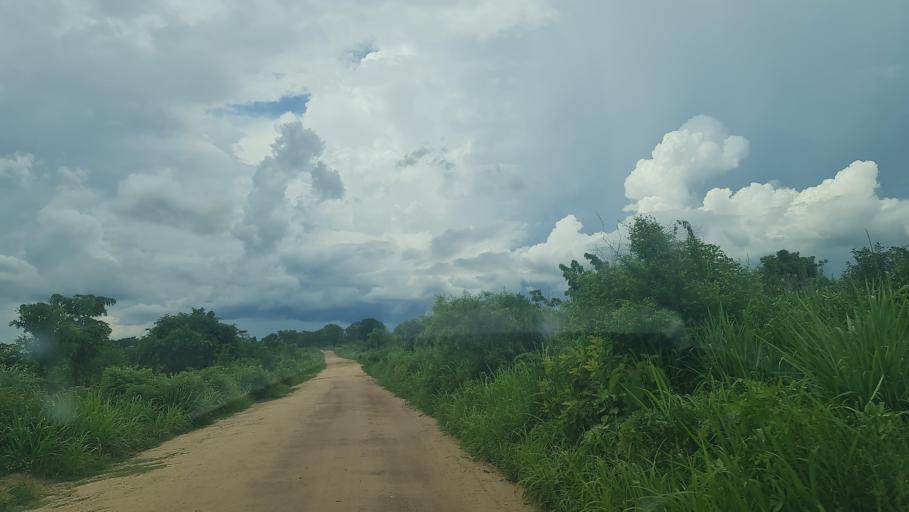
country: MW
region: Southern Region
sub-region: Nsanje District
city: Nsanje
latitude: -17.5842
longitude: 35.6659
